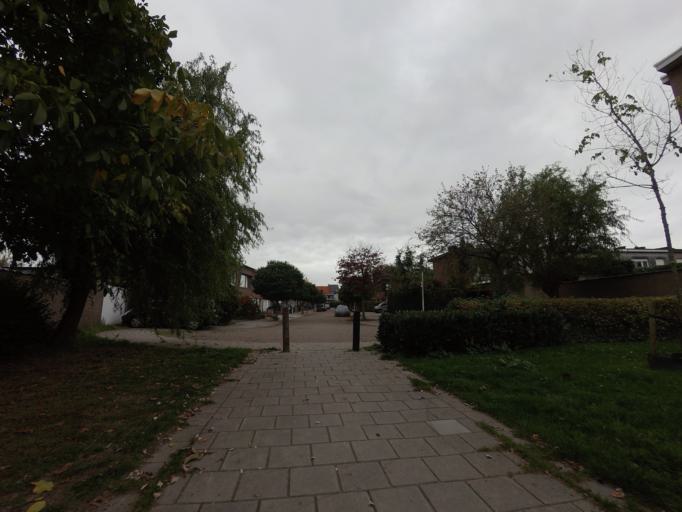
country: BE
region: Flanders
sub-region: Provincie Antwerpen
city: Antwerpen
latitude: 51.2588
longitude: 4.4428
